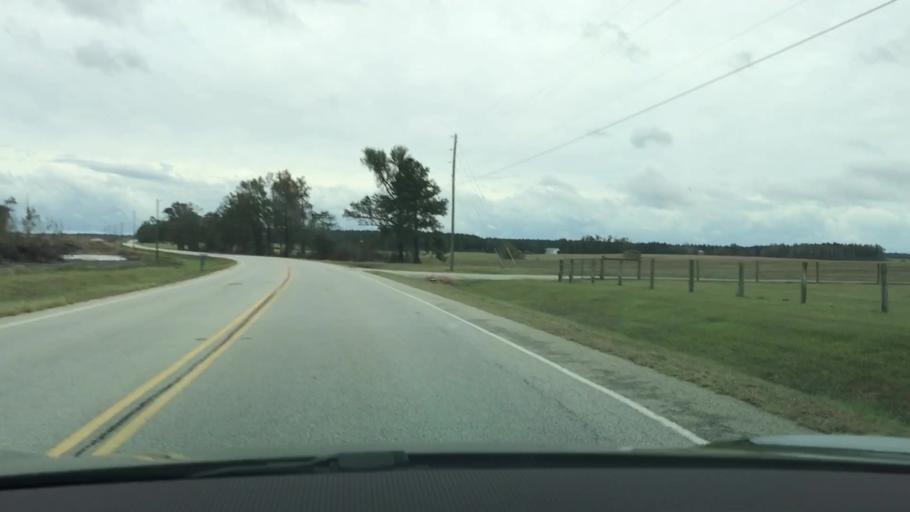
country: US
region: Georgia
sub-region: Jefferson County
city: Wrens
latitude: 33.1191
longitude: -82.4433
